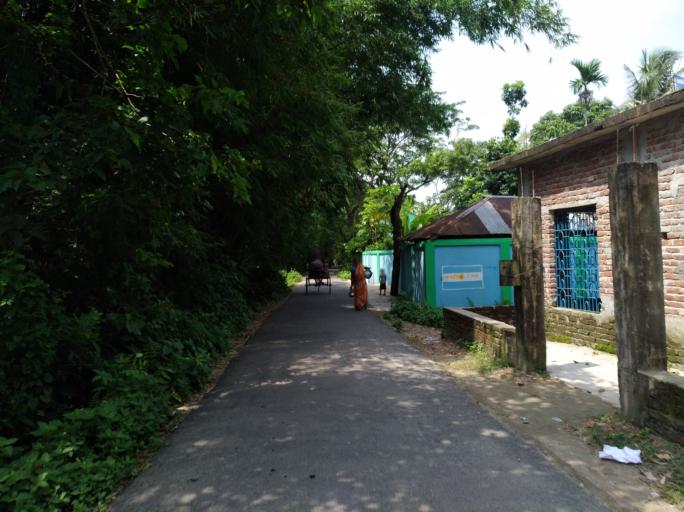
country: BD
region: Dhaka
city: Palang
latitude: 23.2517
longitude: 90.3105
